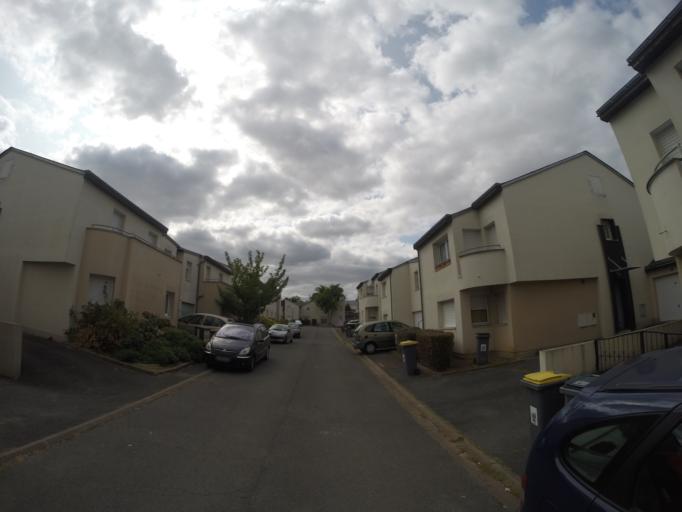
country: FR
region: Centre
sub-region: Departement d'Indre-et-Loire
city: Tours
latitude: 47.4097
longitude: 0.7060
